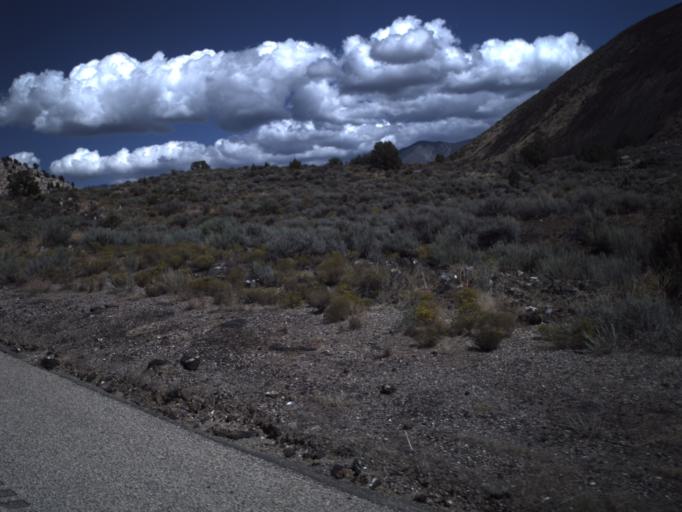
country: US
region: Utah
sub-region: Washington County
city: Ivins
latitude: 37.2406
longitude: -113.6366
